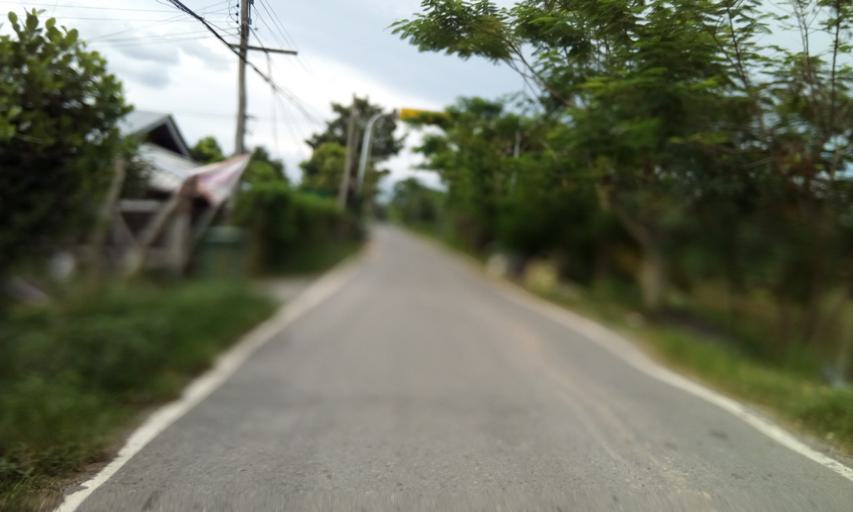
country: TH
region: Pathum Thani
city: Nong Suea
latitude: 14.1281
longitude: 100.8235
